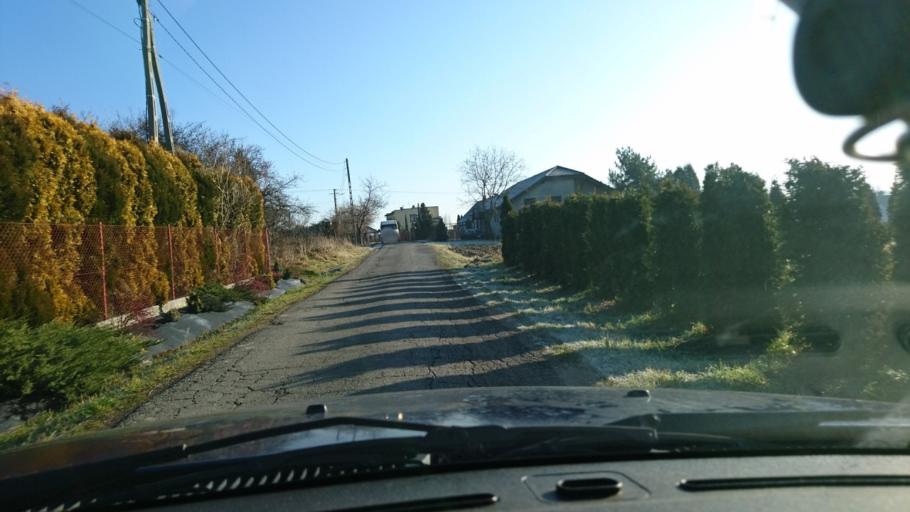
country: PL
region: Silesian Voivodeship
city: Janowice
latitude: 49.8987
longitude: 19.0906
